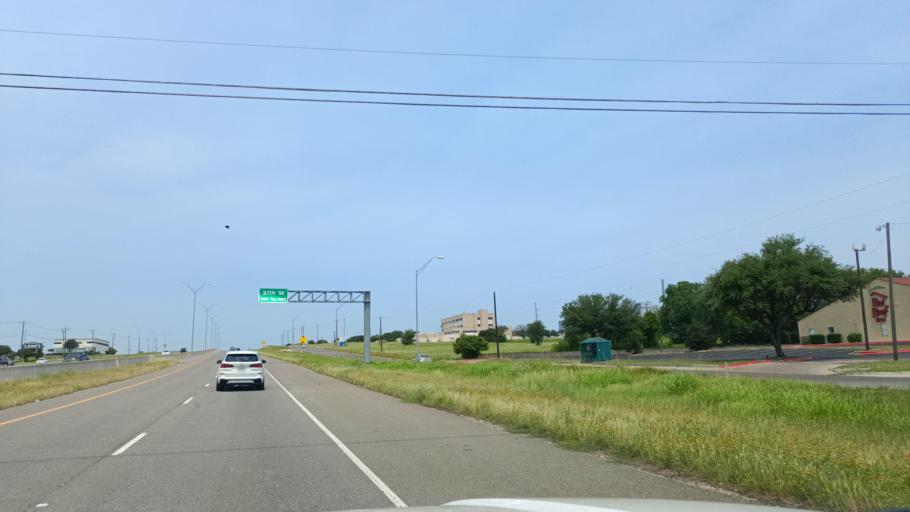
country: US
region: Texas
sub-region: Bell County
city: Temple
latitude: 31.0713
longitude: -97.3587
